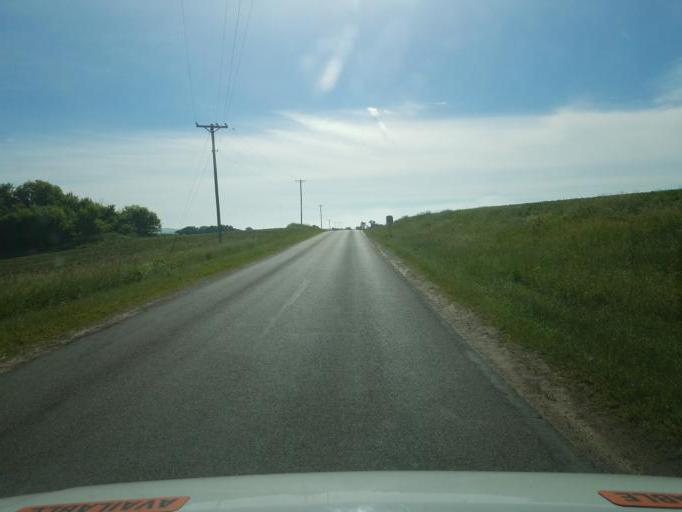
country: US
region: Wisconsin
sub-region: Sauk County
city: Reedsburg
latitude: 43.5396
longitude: -90.0538
